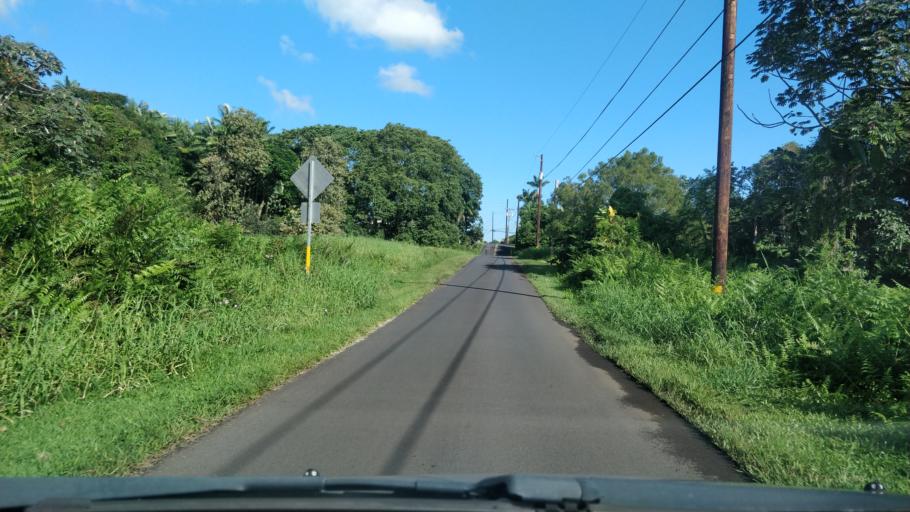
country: US
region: Hawaii
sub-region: Hawaii County
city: Hilo
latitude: 19.6627
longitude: -155.0994
